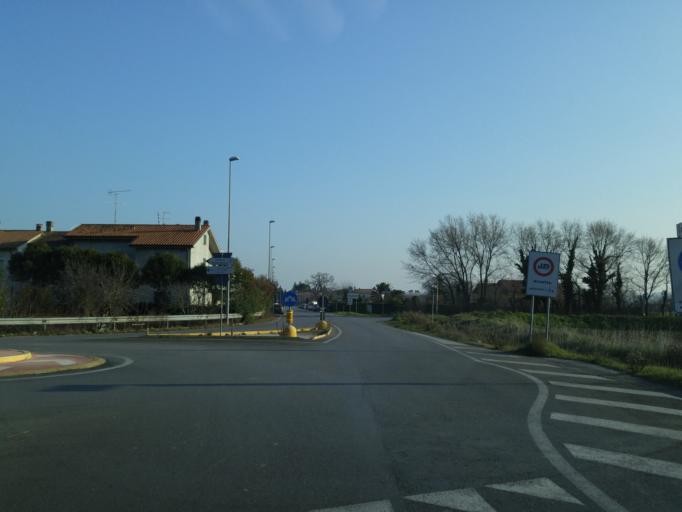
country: IT
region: The Marches
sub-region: Provincia di Pesaro e Urbino
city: Rosciano
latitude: 43.8047
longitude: 12.9871
